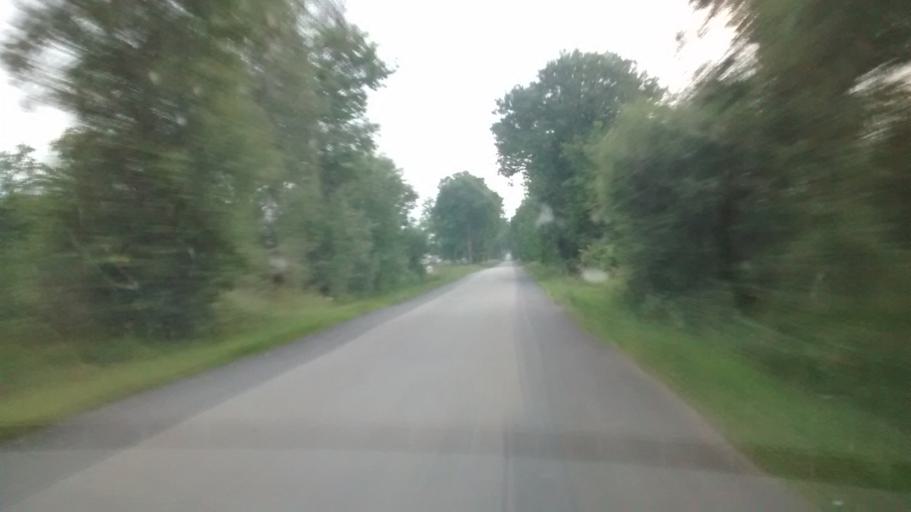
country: FR
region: Brittany
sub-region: Departement du Morbihan
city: Pluherlin
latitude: 47.7331
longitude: -2.3227
